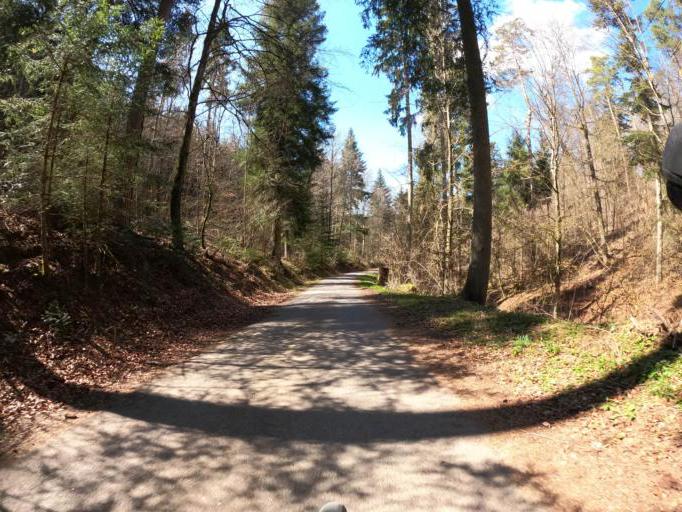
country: DE
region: Baden-Wuerttemberg
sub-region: Regierungsbezirk Stuttgart
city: Bondorf
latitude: 48.4737
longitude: 8.8519
